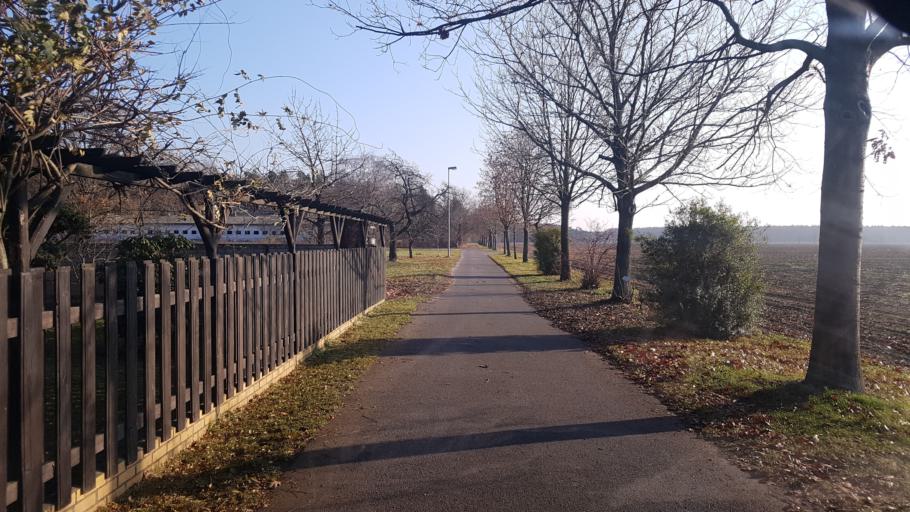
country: DE
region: Brandenburg
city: Tettau
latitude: 51.4367
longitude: 13.7326
